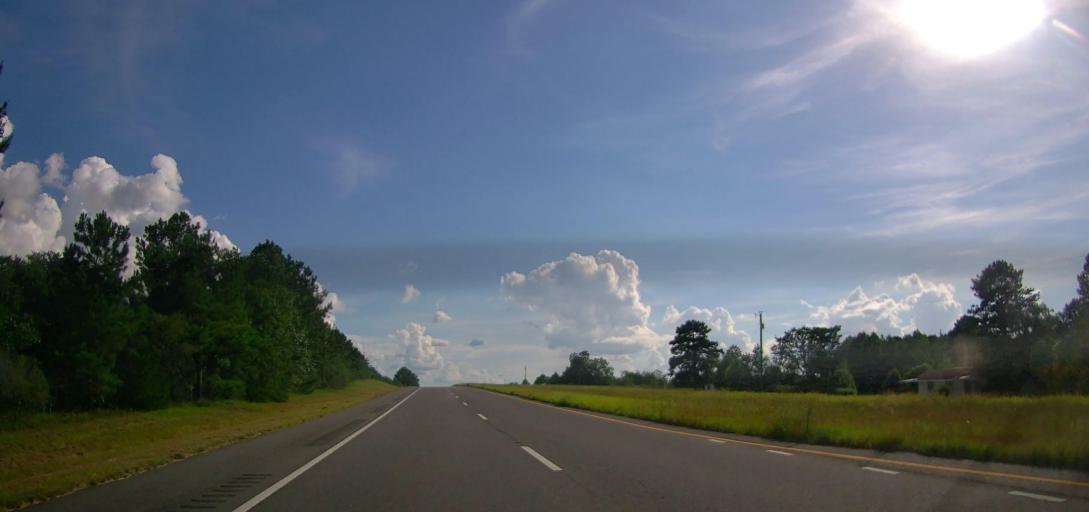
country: US
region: Georgia
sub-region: Talbot County
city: Talbotton
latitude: 32.5984
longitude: -84.4905
